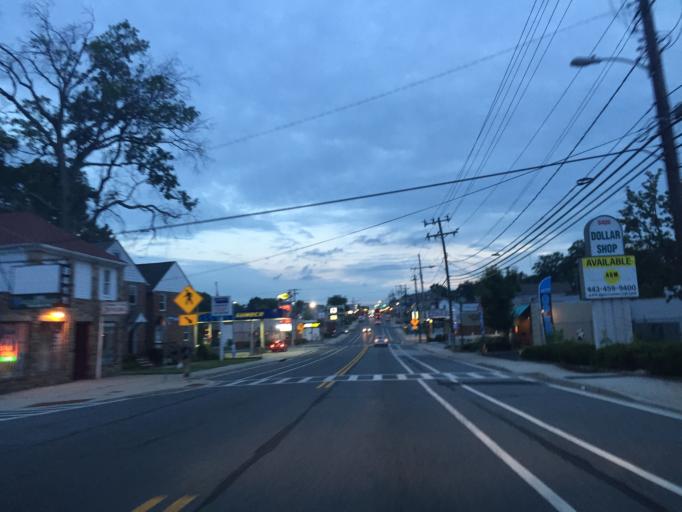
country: US
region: Maryland
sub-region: Baltimore County
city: Parkville
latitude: 39.3811
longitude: -76.5366
